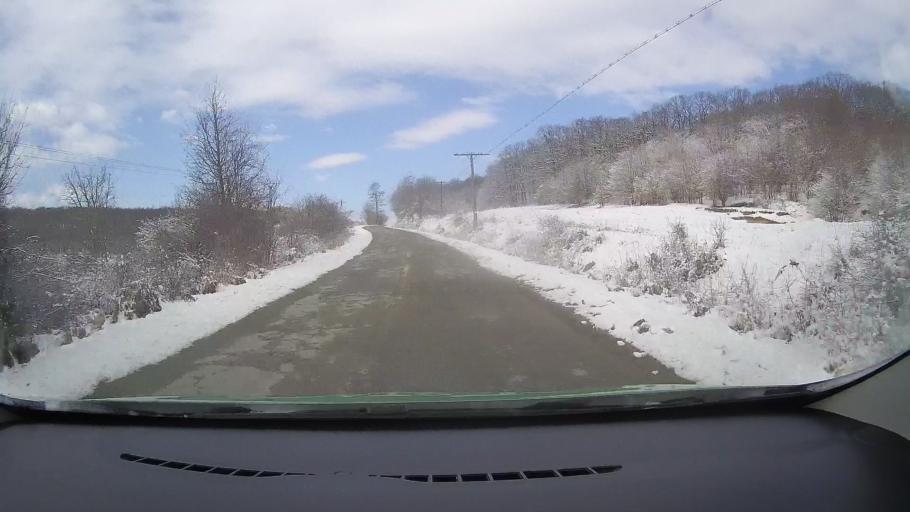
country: RO
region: Sibiu
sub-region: Comuna Altina
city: Altina
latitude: 45.9955
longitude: 24.4282
